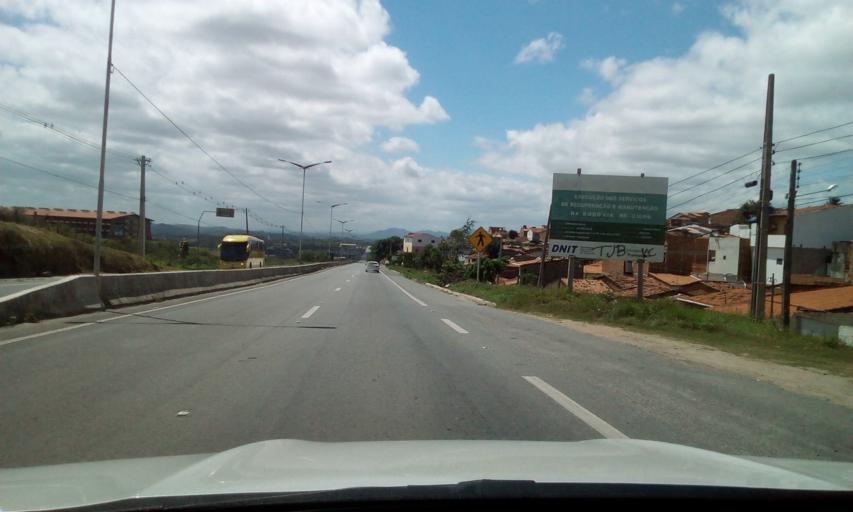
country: BR
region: Paraiba
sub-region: Campina Grande
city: Campina Grande
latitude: -7.2379
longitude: -35.8662
